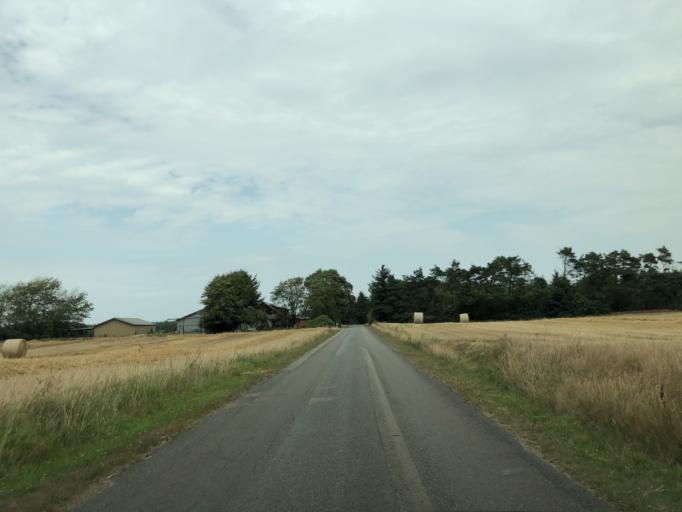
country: DK
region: Central Jutland
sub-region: Holstebro Kommune
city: Ulfborg
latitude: 56.2124
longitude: 8.3181
